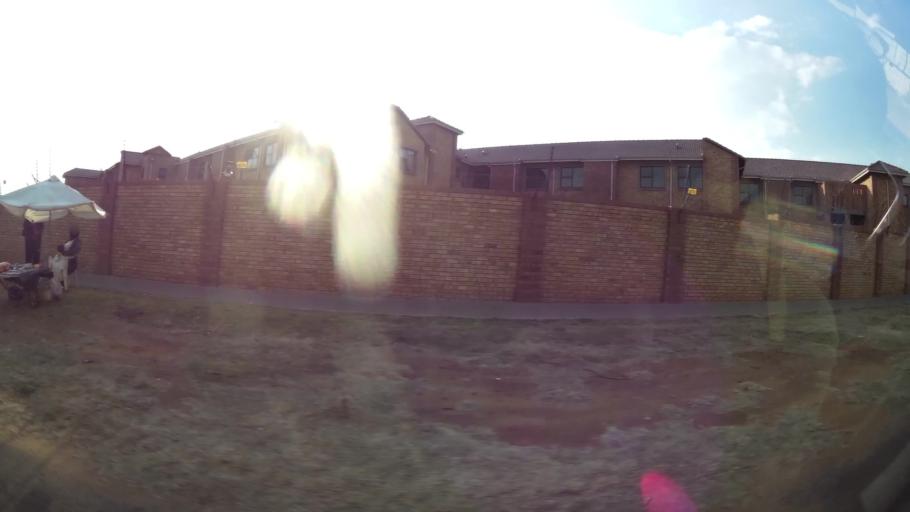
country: ZA
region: Gauteng
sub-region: Ekurhuleni Metropolitan Municipality
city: Benoni
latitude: -26.1160
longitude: 28.2852
